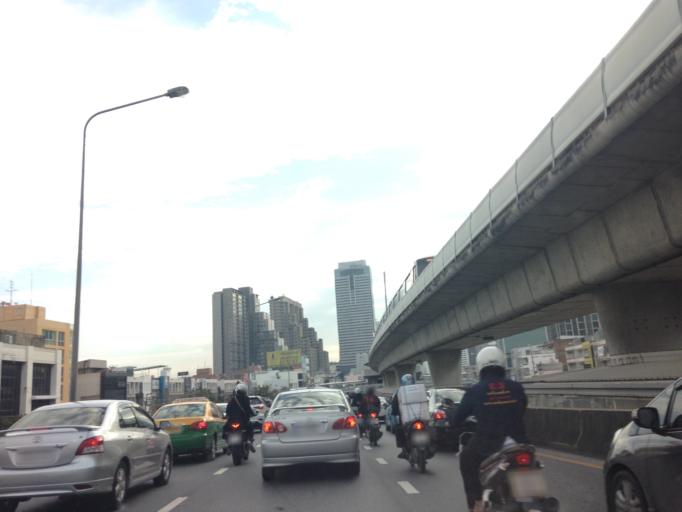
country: TH
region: Bangkok
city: Thon Buri
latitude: 13.7211
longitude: 100.4922
